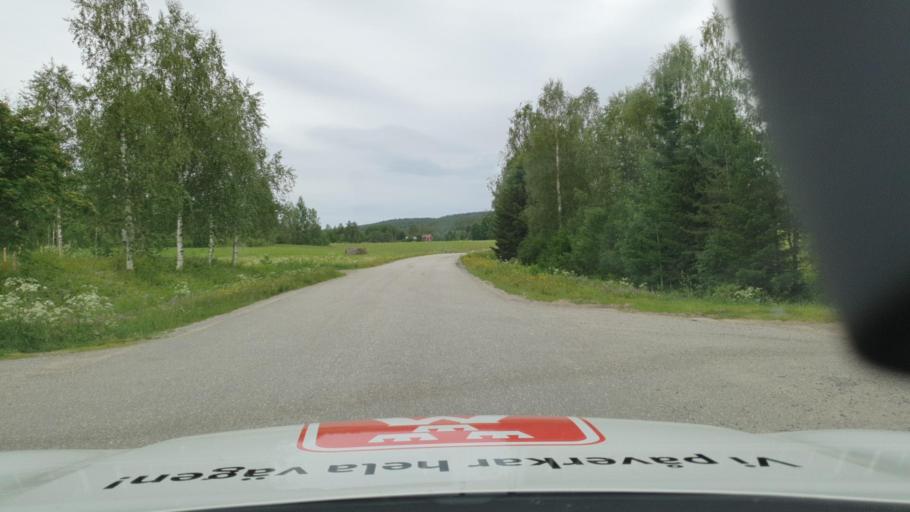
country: SE
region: Vaesterbotten
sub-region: Skelleftea Kommun
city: Burtraesk
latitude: 64.3027
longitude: 20.6492
